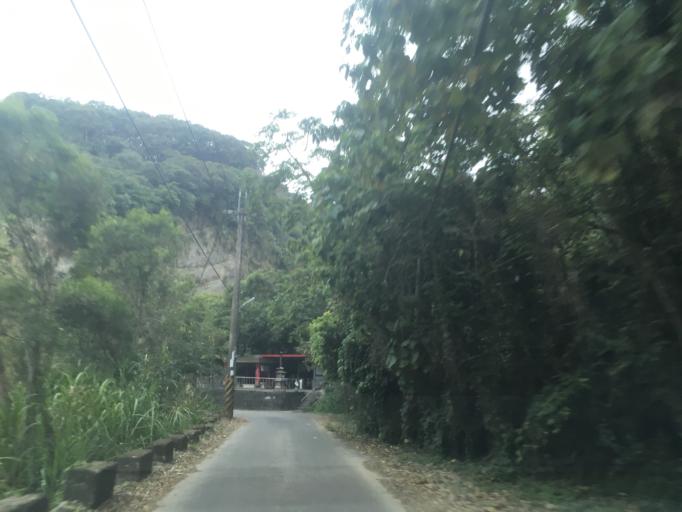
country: TW
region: Taiwan
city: Zhongxing New Village
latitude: 24.0372
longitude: 120.7598
